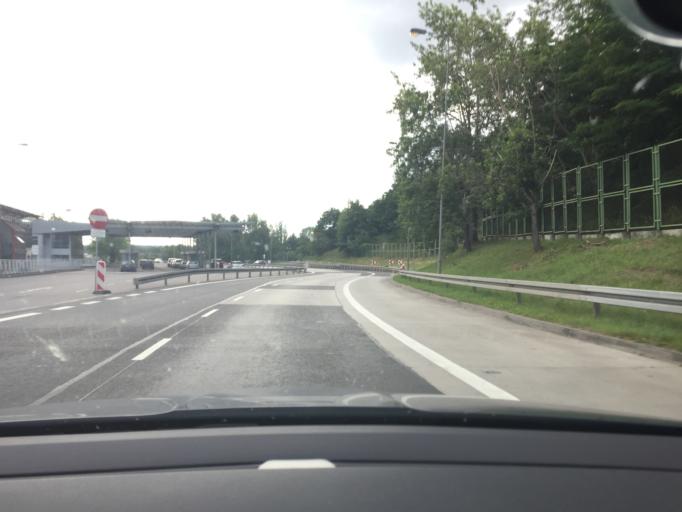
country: PL
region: Lubusz
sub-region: Powiat slubicki
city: Slubice
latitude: 52.3172
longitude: 14.5910
